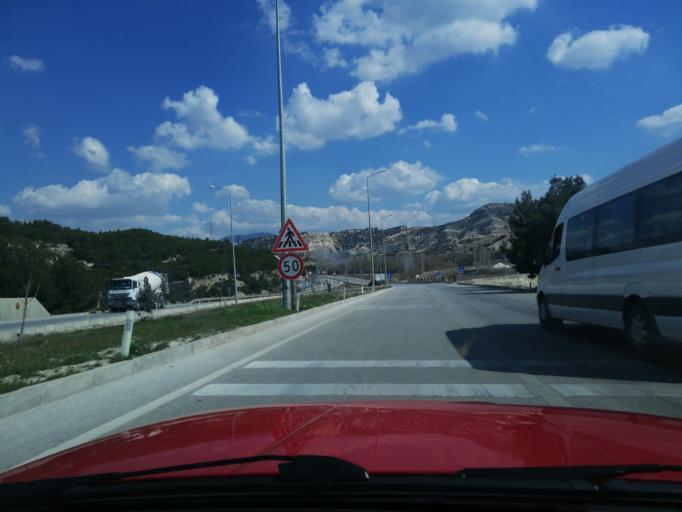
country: TR
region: Burdur
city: Burdur
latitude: 37.7004
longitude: 30.3183
